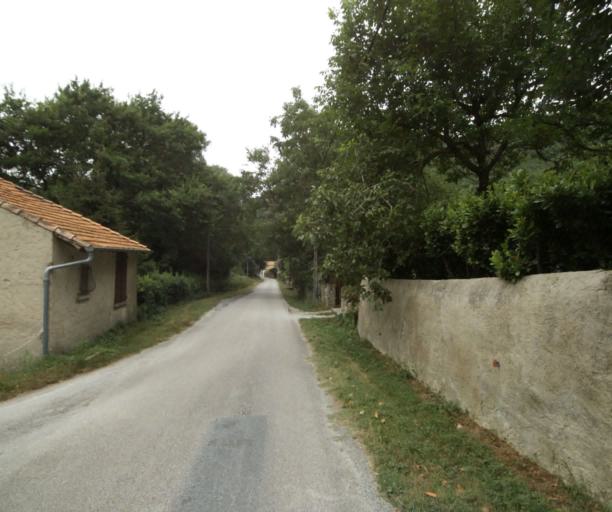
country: FR
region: Midi-Pyrenees
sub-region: Departement du Tarn
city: Soreze
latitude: 43.4366
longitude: 2.0717
